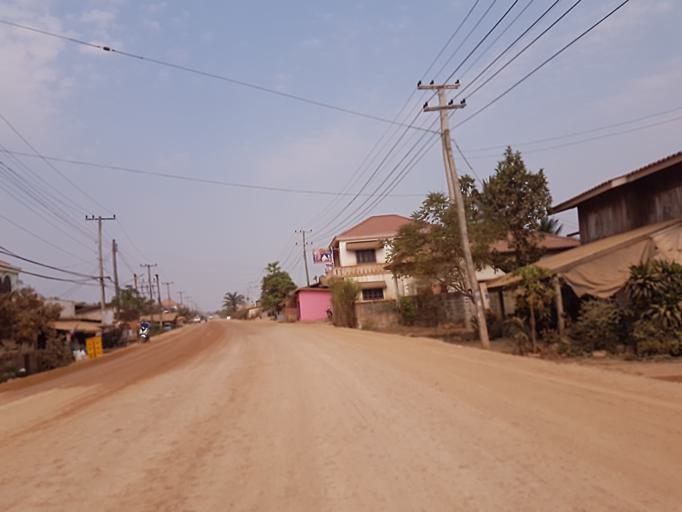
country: TH
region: Nong Khai
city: Nong Khai
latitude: 17.8935
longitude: 102.7488
